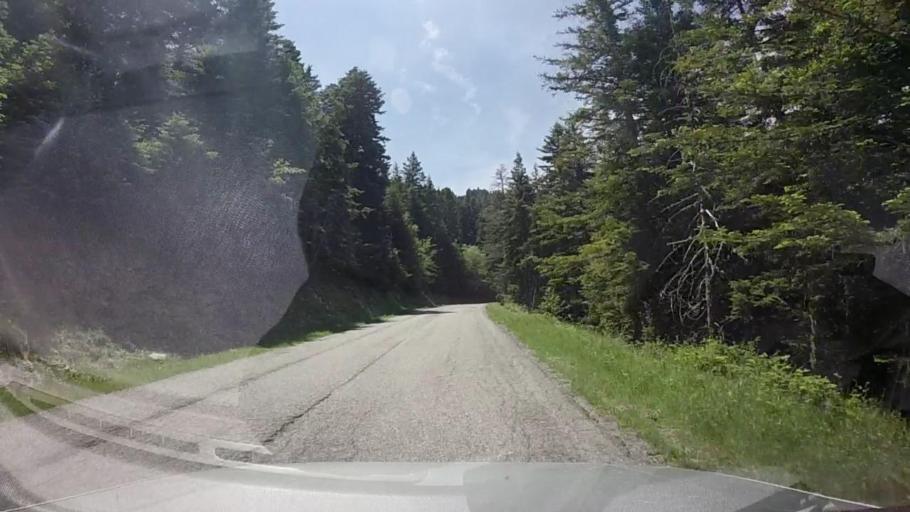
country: FR
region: Provence-Alpes-Cote d'Azur
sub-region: Departement des Alpes-de-Haute-Provence
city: Seyne-les-Alpes
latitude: 44.3475
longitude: 6.3003
